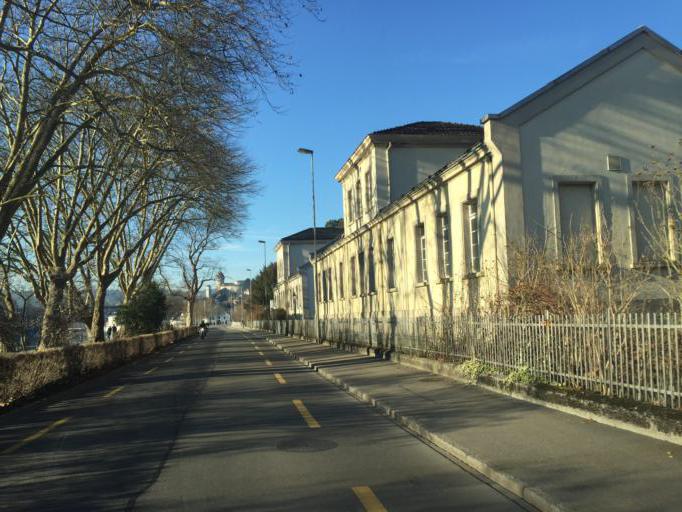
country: CH
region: Zurich
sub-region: Bezirk Andelfingen
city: Feuerthalen
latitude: 47.6933
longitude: 8.6499
